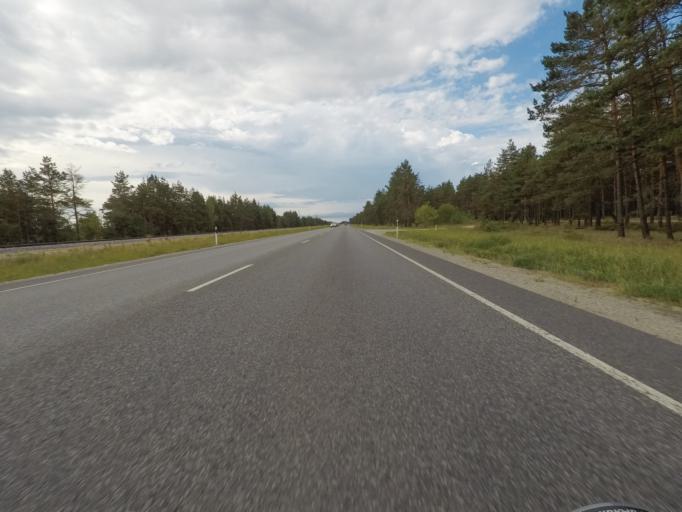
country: EE
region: Harju
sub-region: Saku vald
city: Saku
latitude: 59.3524
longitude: 24.7100
